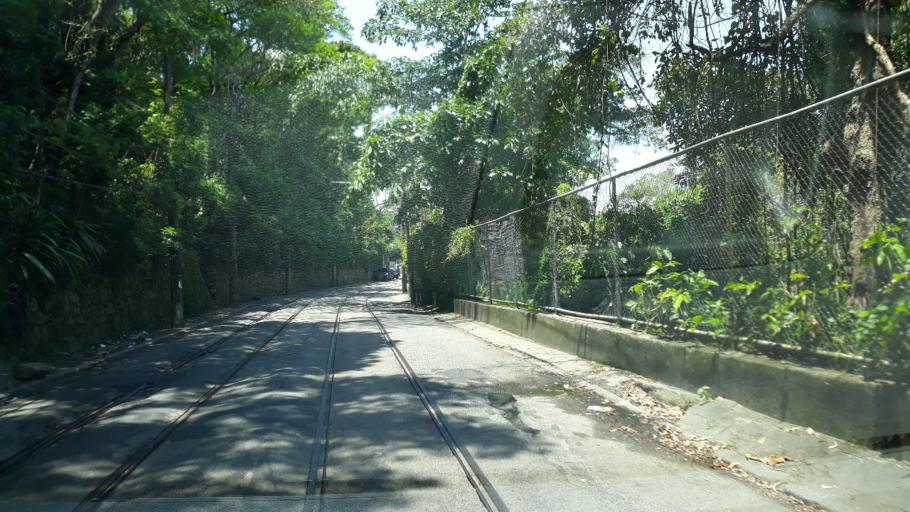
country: BR
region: Rio de Janeiro
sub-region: Rio De Janeiro
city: Rio de Janeiro
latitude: -22.9354
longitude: -43.2024
